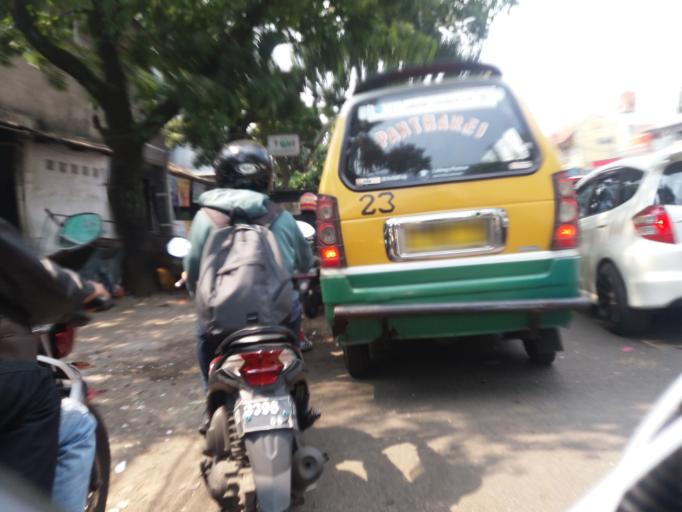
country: ID
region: West Java
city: Bandung
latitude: -6.9162
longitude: 107.5880
